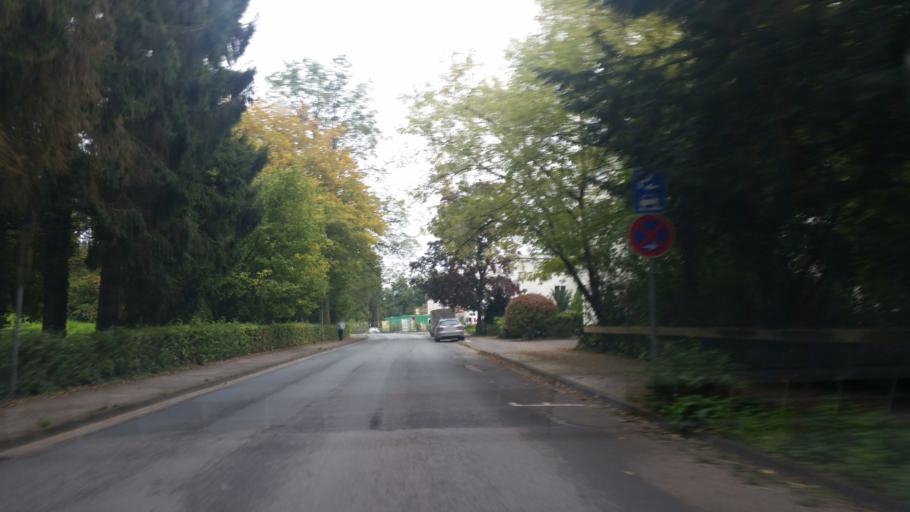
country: DE
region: Lower Saxony
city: Bad Pyrmont
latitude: 51.9898
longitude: 9.2537
